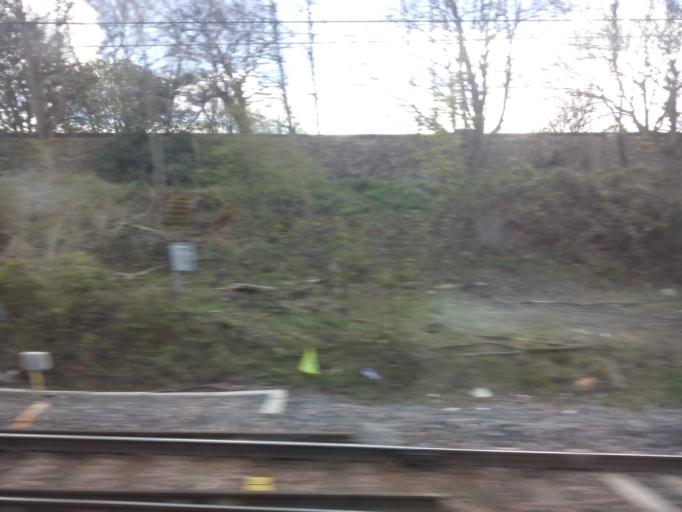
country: GB
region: Scotland
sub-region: West Lothian
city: Seafield
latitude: 55.9558
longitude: -3.1368
